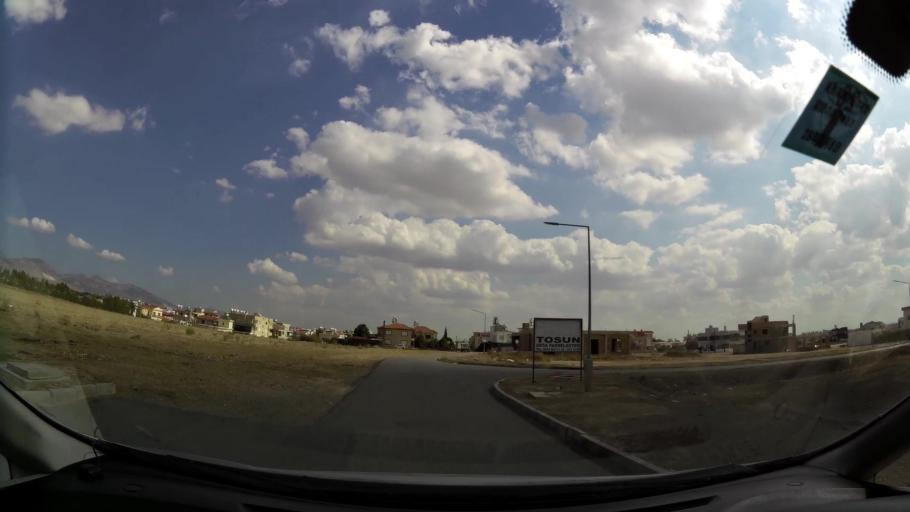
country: CY
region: Lefkosia
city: Nicosia
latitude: 35.2186
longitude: 33.2910
